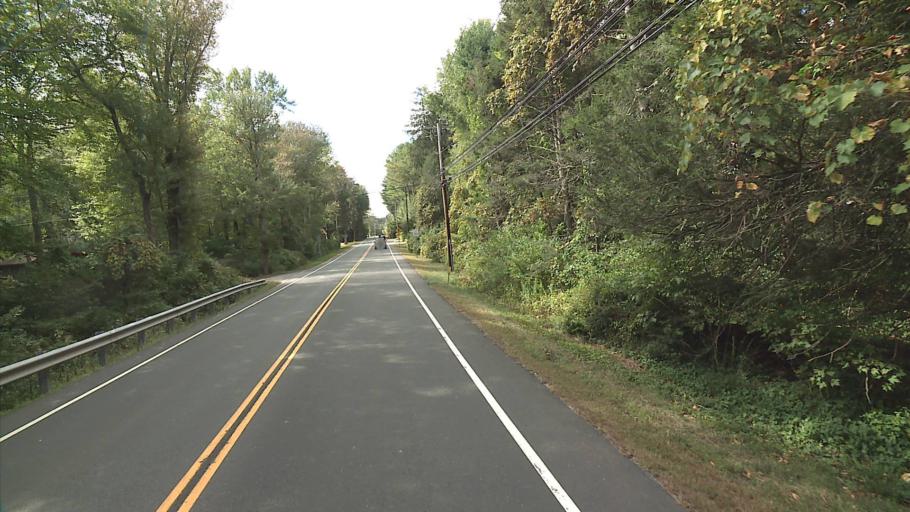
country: US
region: Connecticut
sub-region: Middlesex County
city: Chester Center
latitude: 41.3995
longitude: -72.4941
